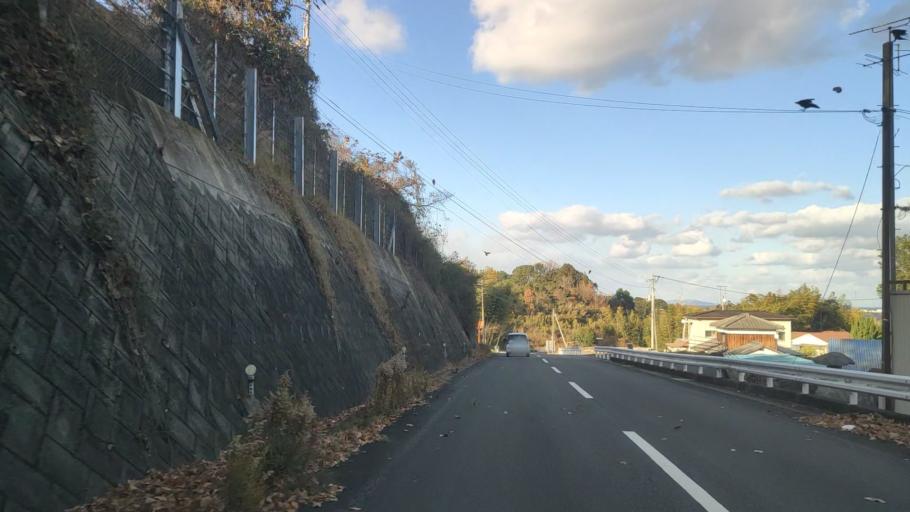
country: JP
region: Ehime
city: Saijo
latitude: 33.8863
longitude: 133.1291
